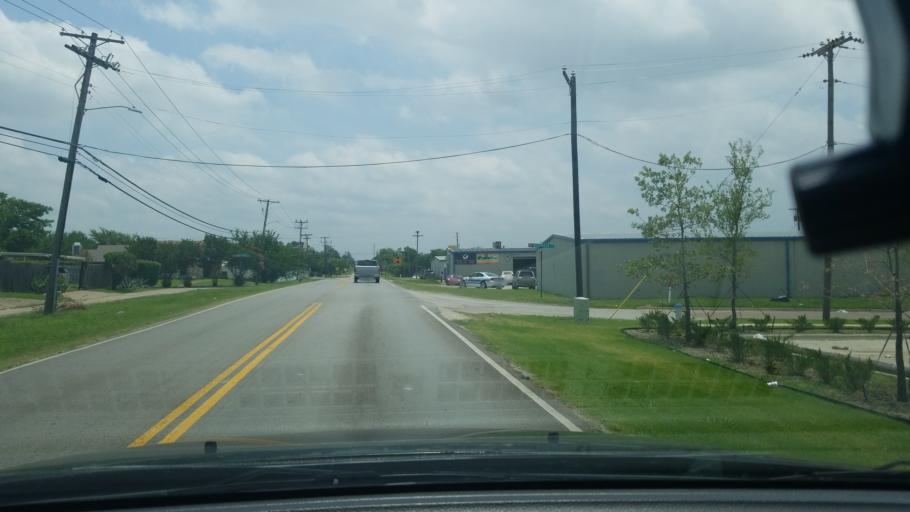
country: US
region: Texas
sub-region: Dallas County
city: Mesquite
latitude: 32.7965
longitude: -96.6173
